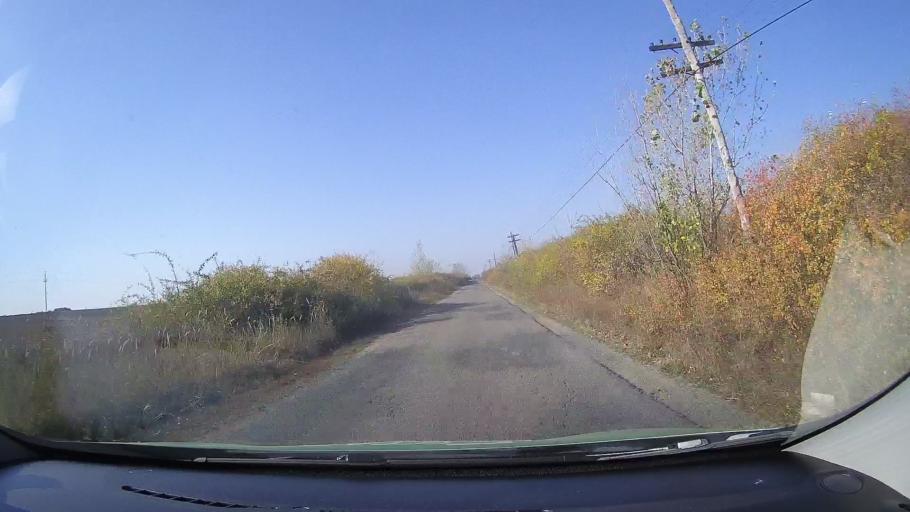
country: RO
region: Satu Mare
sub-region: Comuna Sauca
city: Sauca
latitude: 47.4688
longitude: 22.5108
